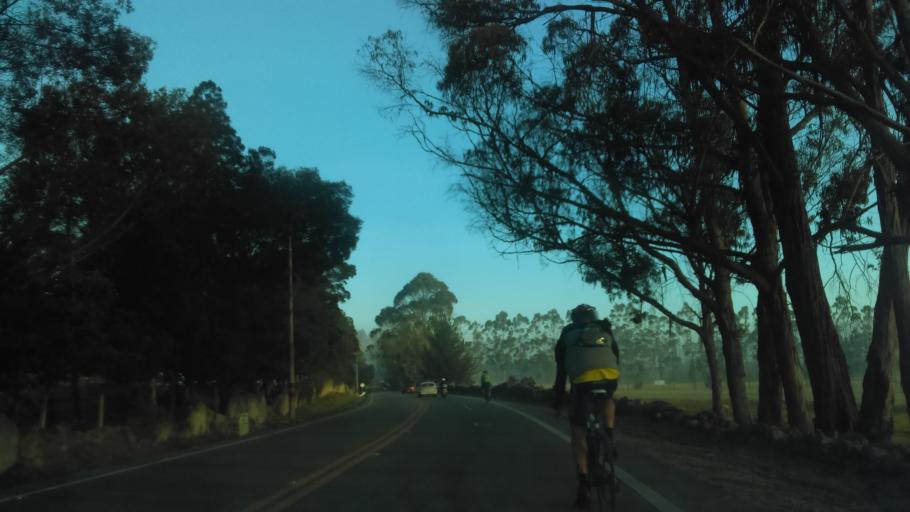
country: CO
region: Cundinamarca
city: Soacha
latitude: 4.6041
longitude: -74.2793
